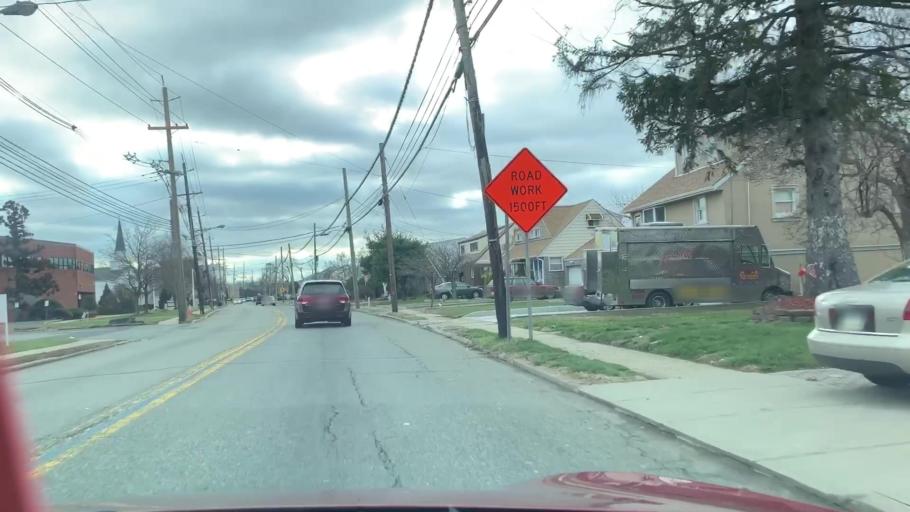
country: US
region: New Jersey
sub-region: Bergen County
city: Moonachie
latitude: 40.8382
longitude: -74.0504
